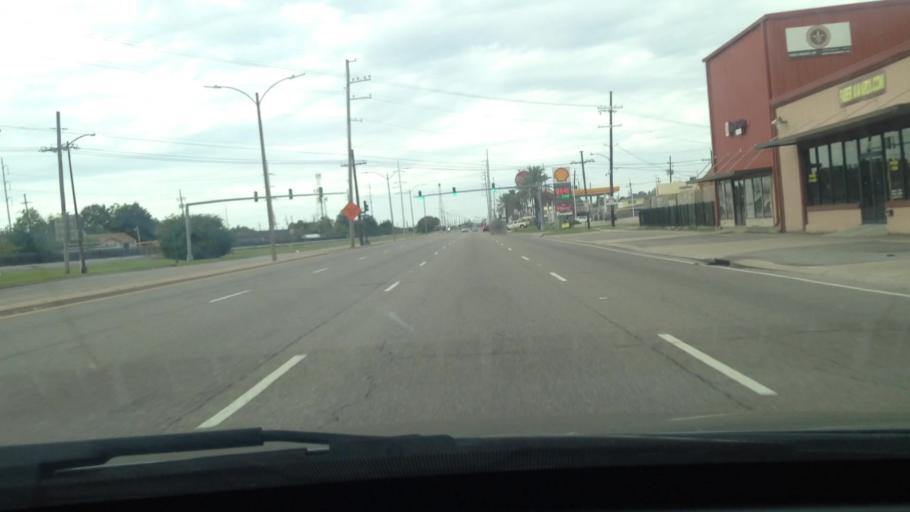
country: US
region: Louisiana
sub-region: Jefferson Parish
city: Jefferson
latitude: 29.9718
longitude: -90.1194
